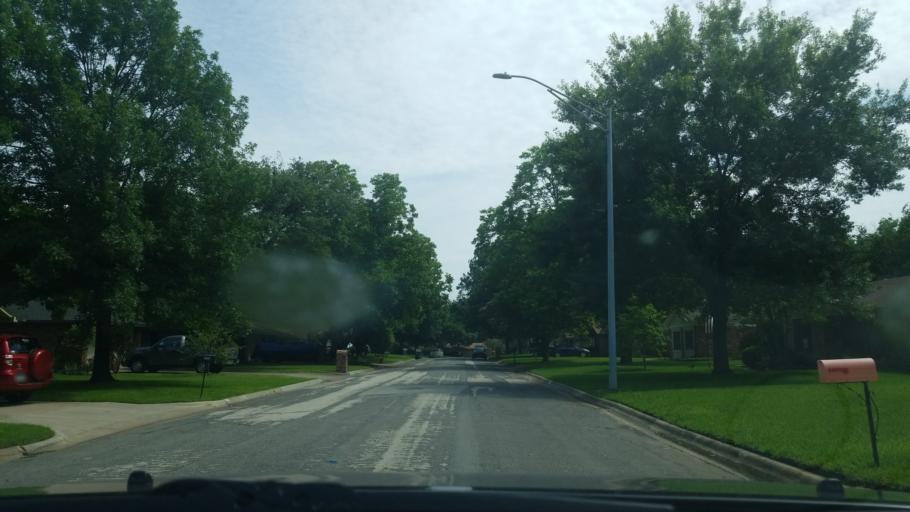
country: US
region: Texas
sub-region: Denton County
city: Denton
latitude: 33.2348
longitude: -97.1494
